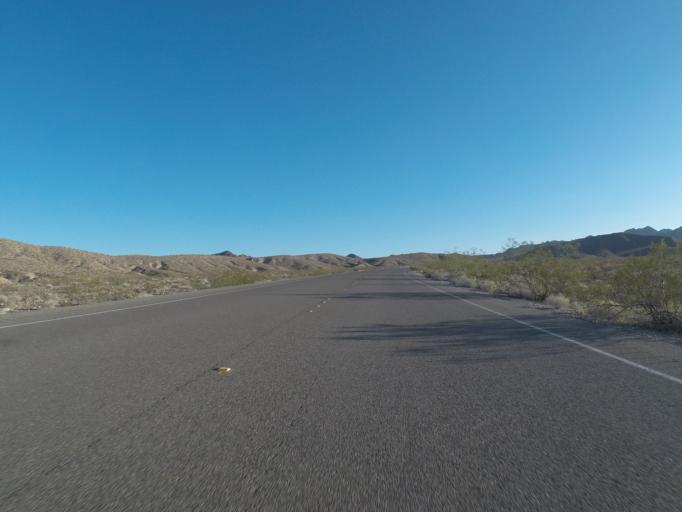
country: US
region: Nevada
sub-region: Clark County
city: Moapa Valley
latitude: 36.2814
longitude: -114.4888
